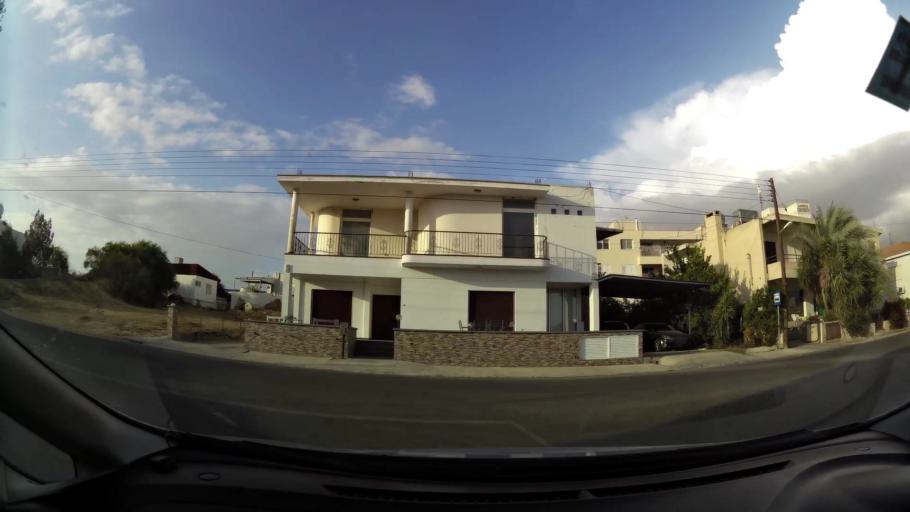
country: CY
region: Lefkosia
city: Nicosia
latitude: 35.1627
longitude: 33.3908
